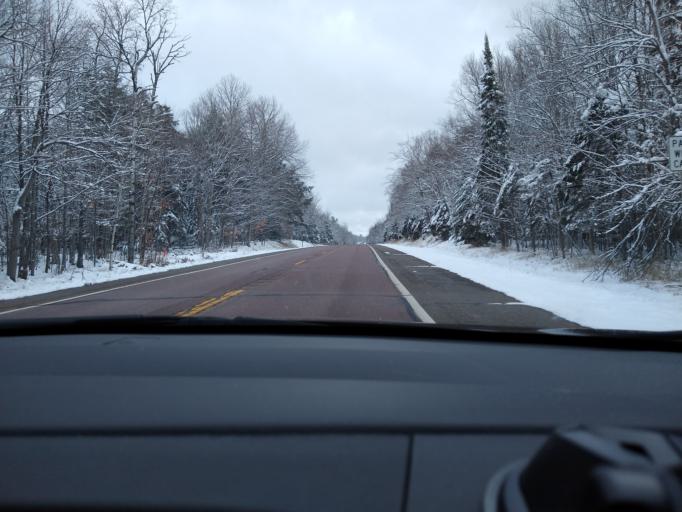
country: US
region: Michigan
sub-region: Iron County
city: Iron River
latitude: 46.1850
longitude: -88.9745
